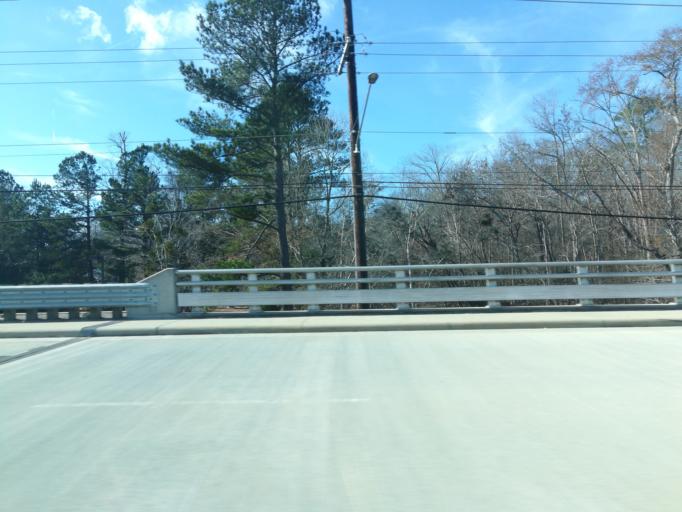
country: US
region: North Carolina
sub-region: Nash County
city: Rocky Mount
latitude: 35.9684
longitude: -77.8499
